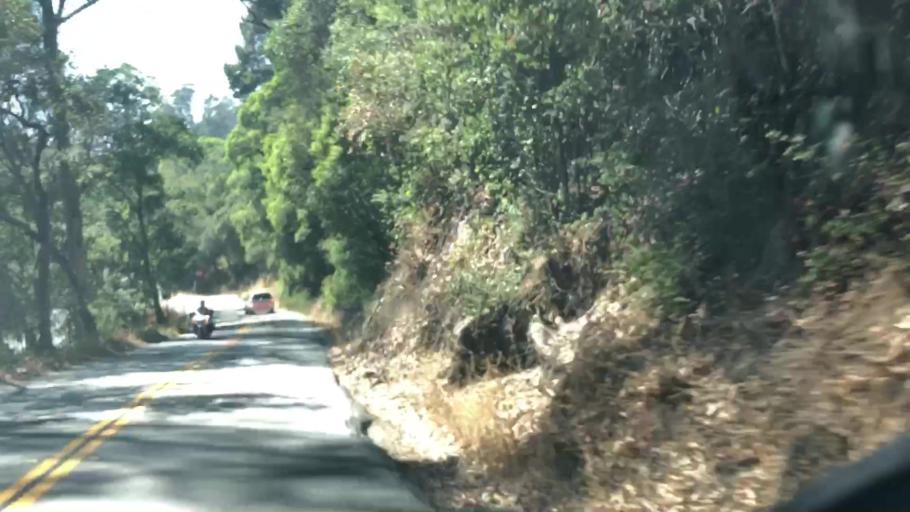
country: US
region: California
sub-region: Santa Cruz County
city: Aptos Hills-Larkin Valley
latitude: 36.9875
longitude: -121.8348
